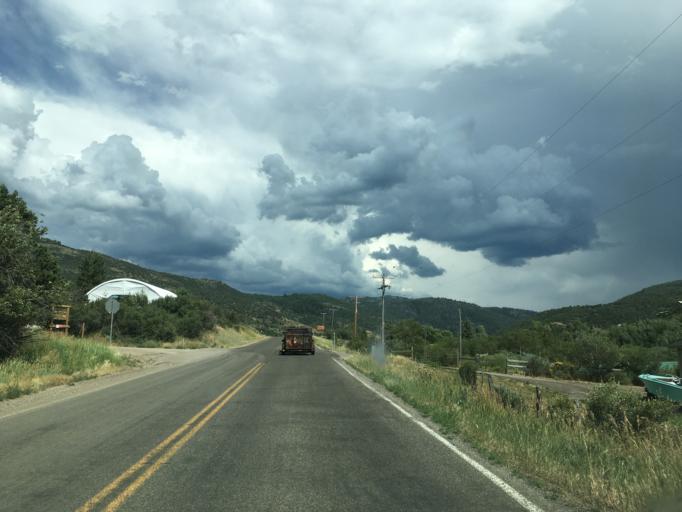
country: US
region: Utah
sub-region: Summit County
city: Francis
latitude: 40.6256
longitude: -111.2391
